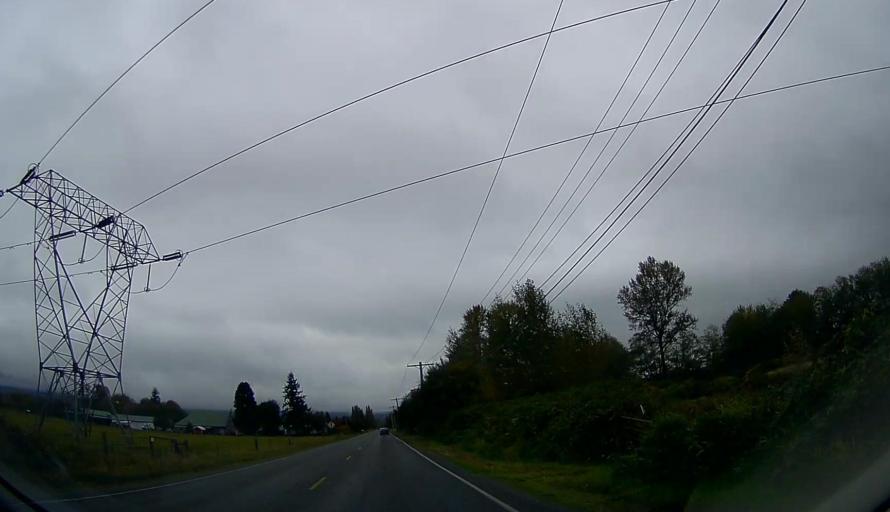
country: US
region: Washington
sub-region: Skagit County
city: Sedro-Woolley
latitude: 48.5091
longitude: -122.2010
